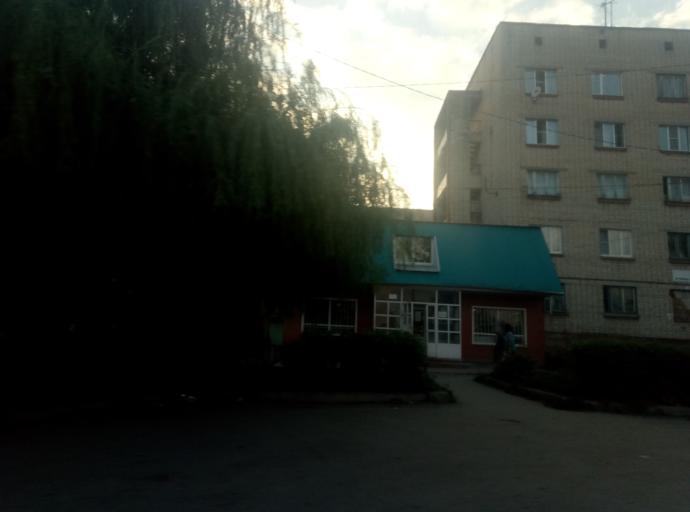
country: RU
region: Tula
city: Kireyevsk
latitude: 53.9212
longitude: 37.9166
